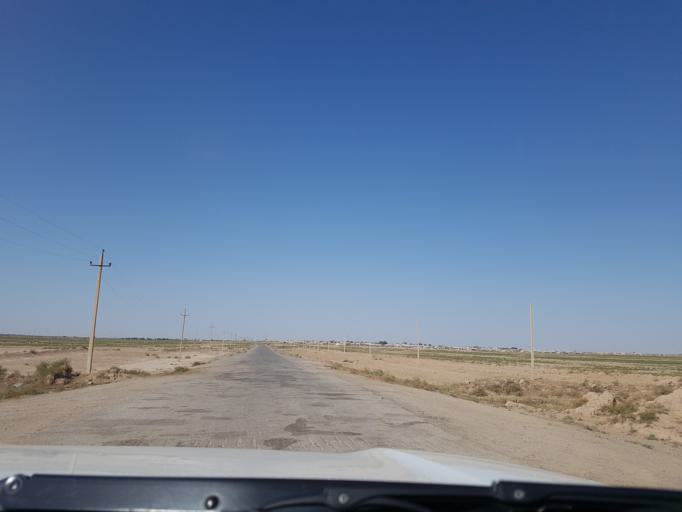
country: IR
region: Razavi Khorasan
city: Sarakhs
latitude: 36.4978
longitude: 61.2537
